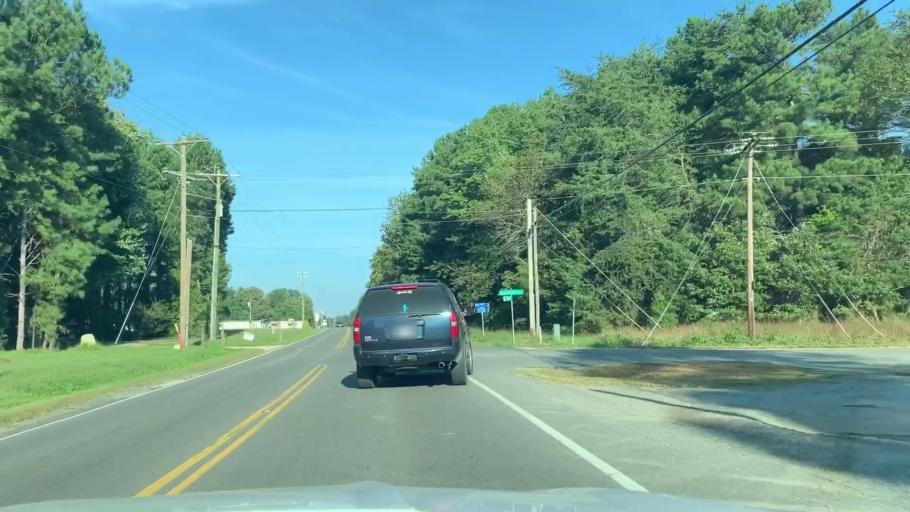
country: US
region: Virginia
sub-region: Lancaster County
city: Lancaster
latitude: 37.7638
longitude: -76.4244
